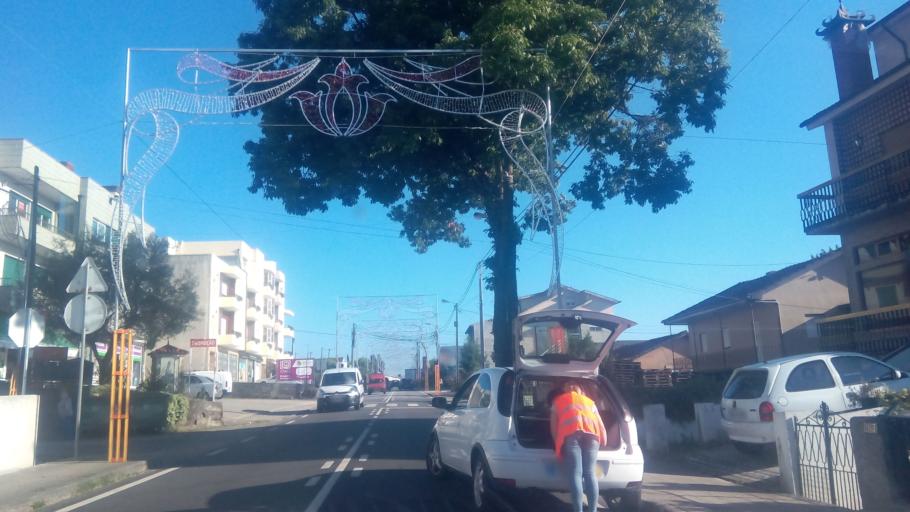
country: PT
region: Porto
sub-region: Pacos de Ferreira
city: Ferreira
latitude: 41.2396
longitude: -8.3631
